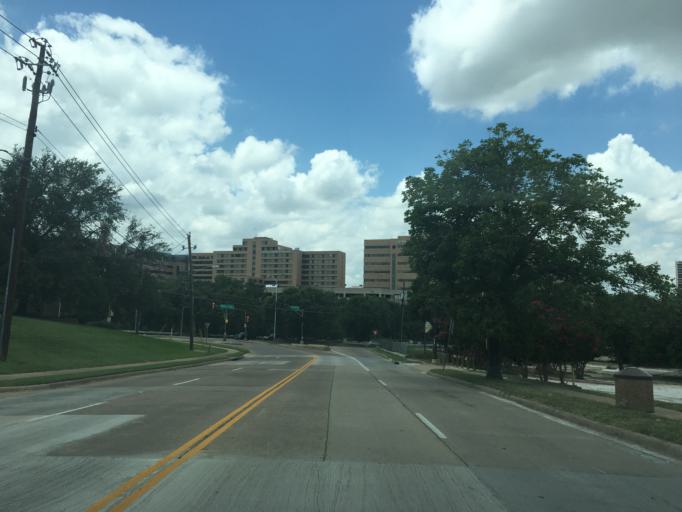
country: US
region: Texas
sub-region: Dallas County
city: University Park
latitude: 32.8793
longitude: -96.7589
